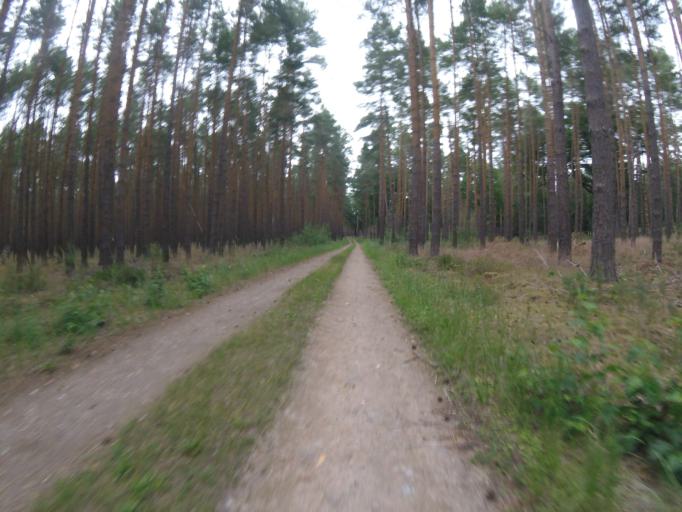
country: DE
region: Brandenburg
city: Gross Koris
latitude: 52.2033
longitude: 13.6763
